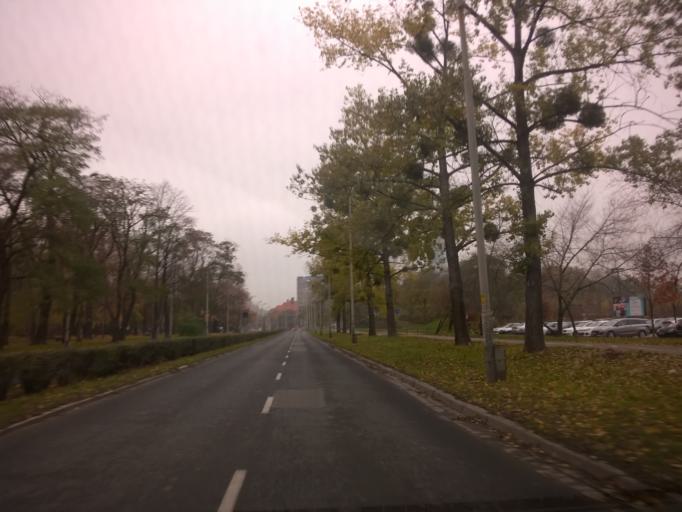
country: PL
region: Lower Silesian Voivodeship
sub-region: Powiat wroclawski
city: Wroclaw
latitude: 51.0888
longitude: 17.0326
